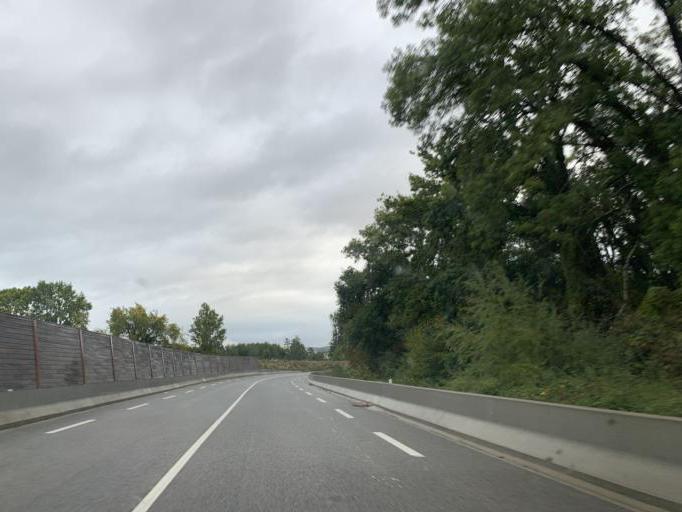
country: FR
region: Rhone-Alpes
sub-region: Departement de l'Ain
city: Belley
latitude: 45.7477
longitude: 5.6903
